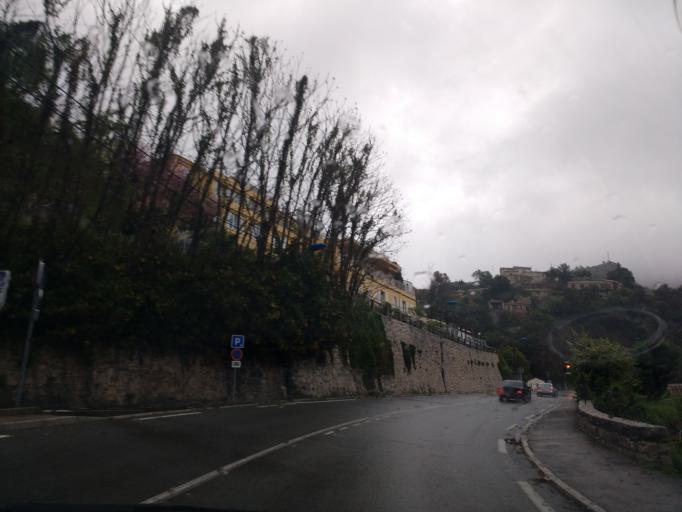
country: FR
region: Provence-Alpes-Cote d'Azur
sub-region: Departement des Alpes-Maritimes
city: Eze
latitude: 43.7249
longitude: 7.3798
